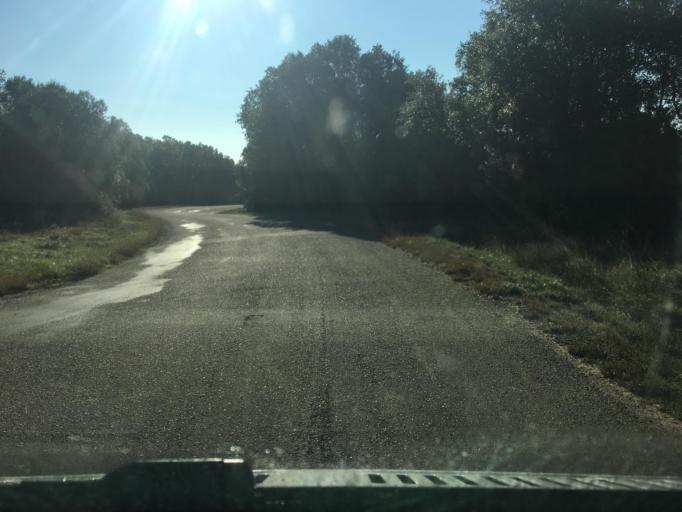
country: FR
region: Languedoc-Roussillon
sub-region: Departement du Gard
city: Goudargues
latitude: 44.1690
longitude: 4.3478
